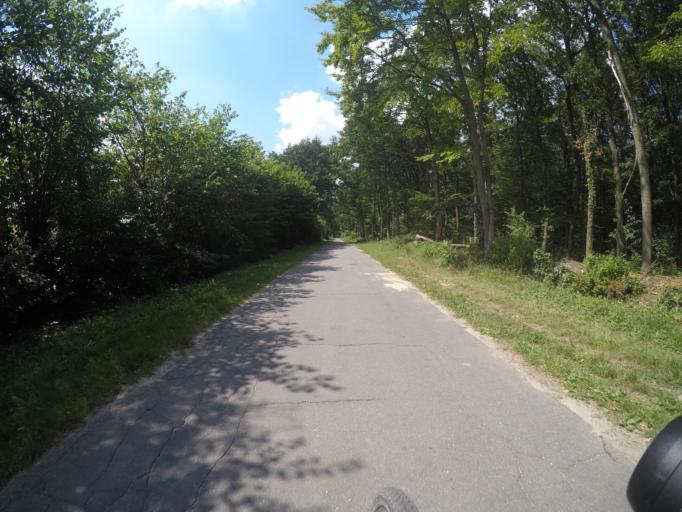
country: DE
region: Schleswig-Holstein
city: Glinde
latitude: 53.5221
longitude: 10.1973
